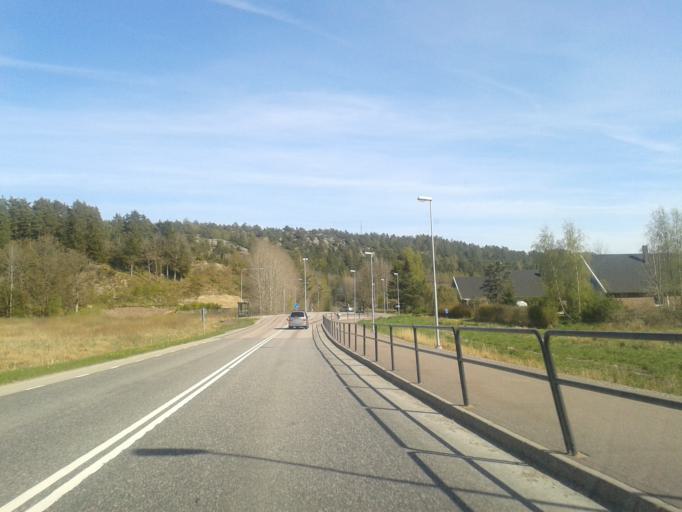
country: SE
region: Vaestra Goetaland
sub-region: Ale Kommun
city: Nodinge-Nol
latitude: 57.8981
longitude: 12.0610
